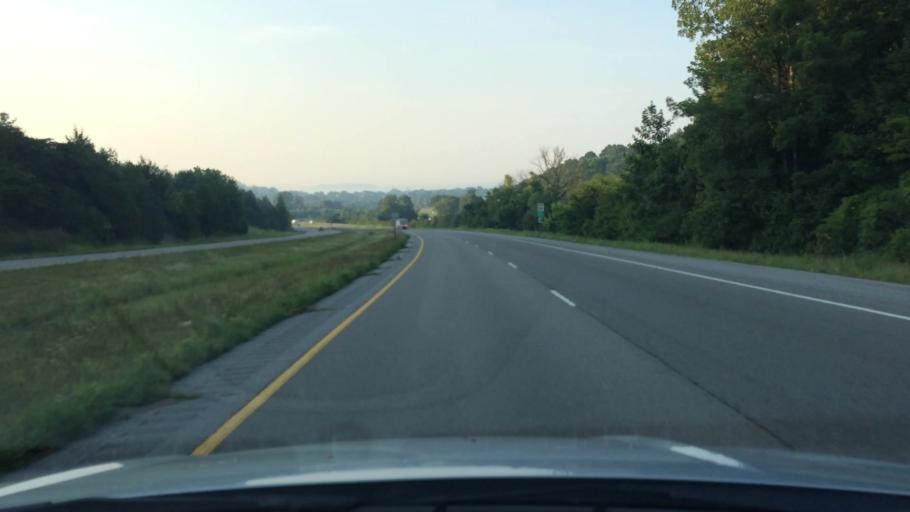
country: US
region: Tennessee
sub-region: Giles County
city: Pulaski
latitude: 35.1763
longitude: -87.0596
